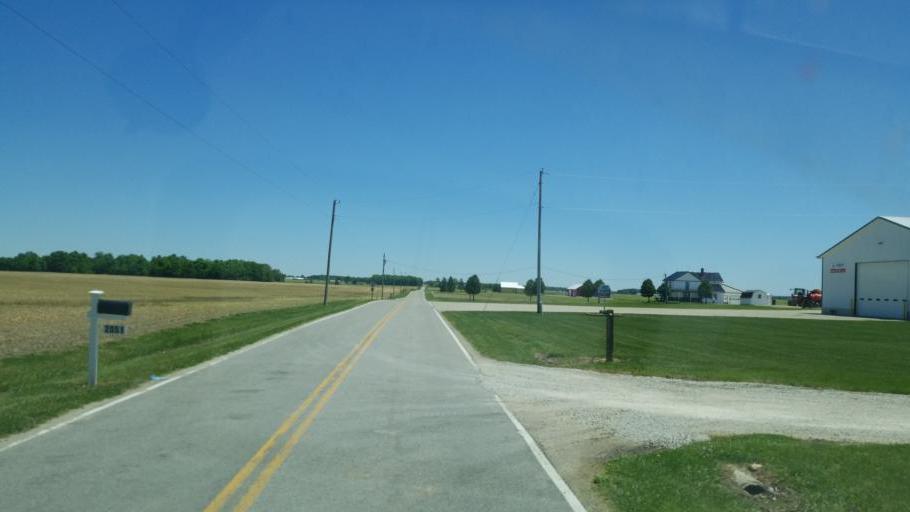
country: US
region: Ohio
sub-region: Darke County
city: Ansonia
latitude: 40.2796
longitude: -84.7274
